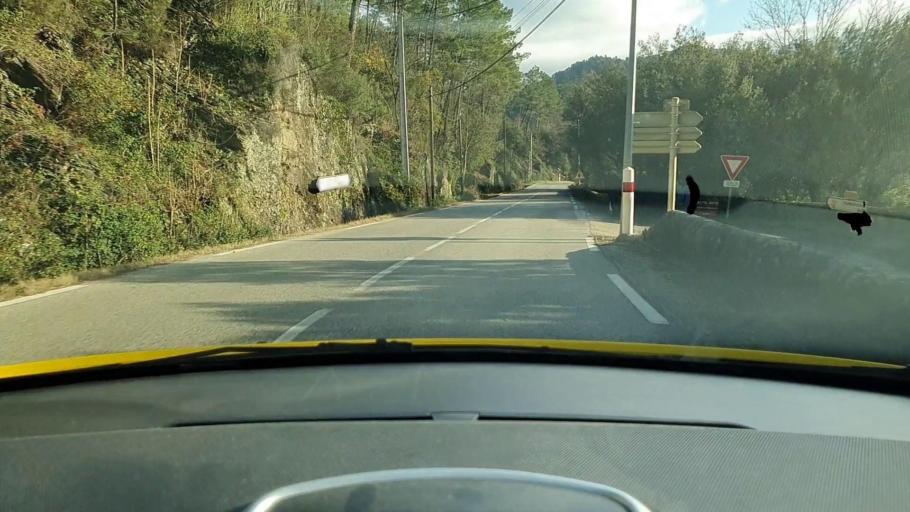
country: FR
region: Languedoc-Roussillon
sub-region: Departement du Gard
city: Branoux-les-Taillades
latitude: 44.3088
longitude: 3.9703
